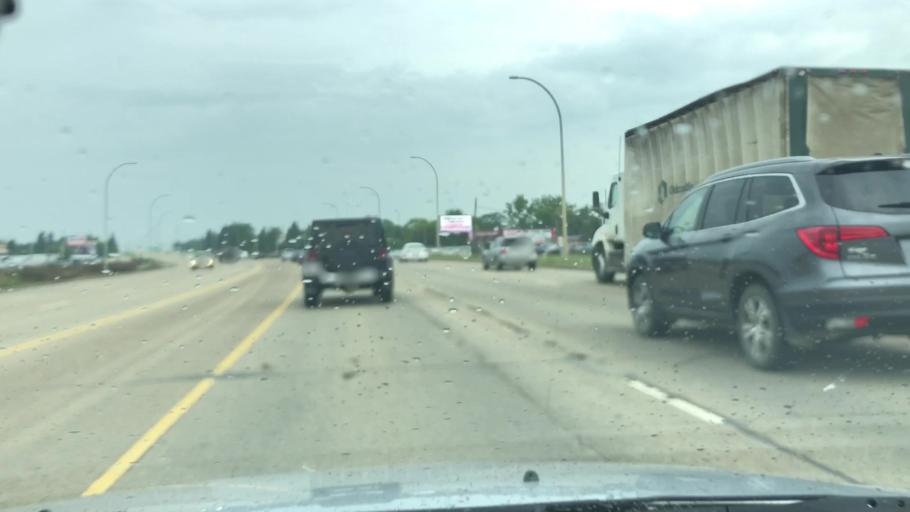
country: CA
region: Alberta
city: St. Albert
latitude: 53.6059
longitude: -113.5803
